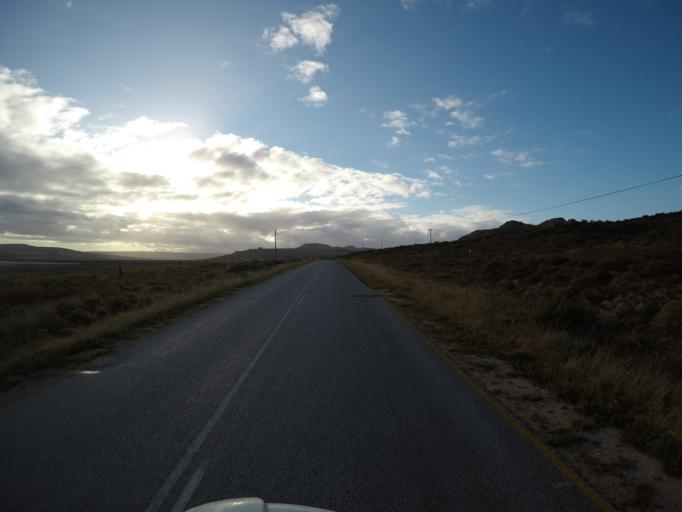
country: ZA
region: Western Cape
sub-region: West Coast District Municipality
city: Clanwilliam
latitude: -32.3244
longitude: 18.3625
